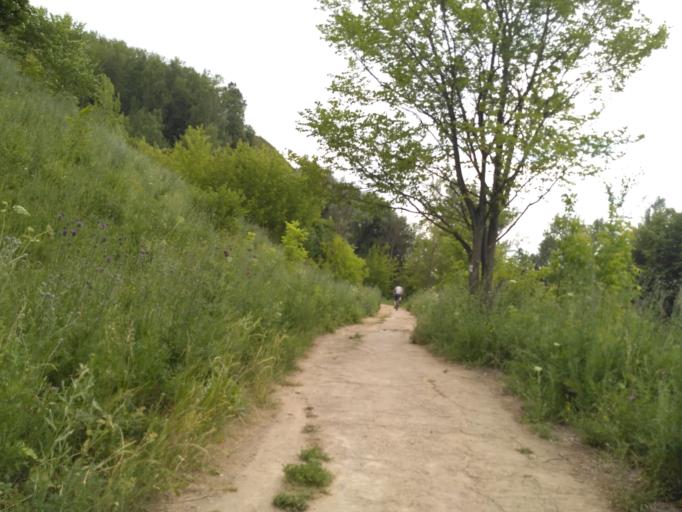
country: RU
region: Nizjnij Novgorod
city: Nizhniy Novgorod
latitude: 56.2773
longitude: 43.9712
